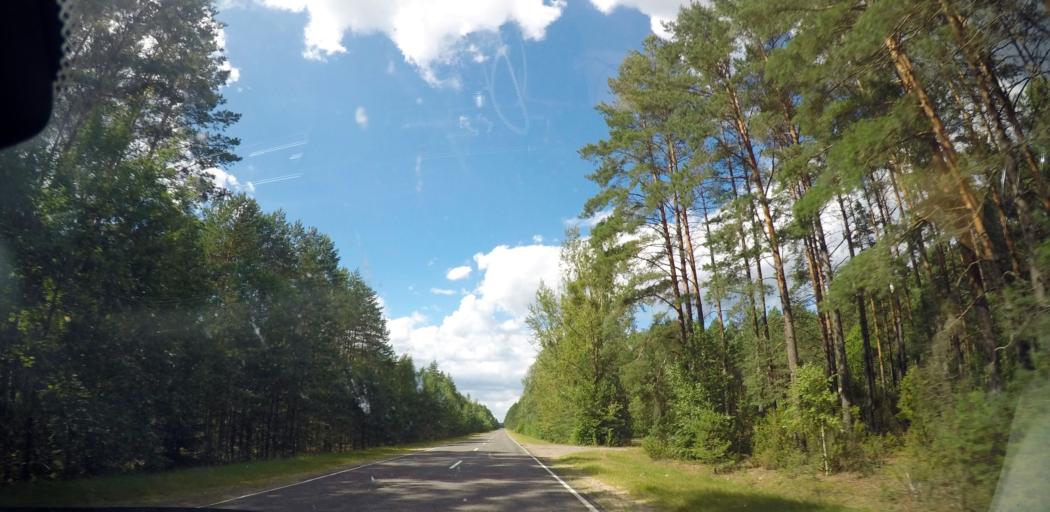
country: LT
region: Alytaus apskritis
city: Druskininkai
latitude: 53.8593
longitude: 24.1808
